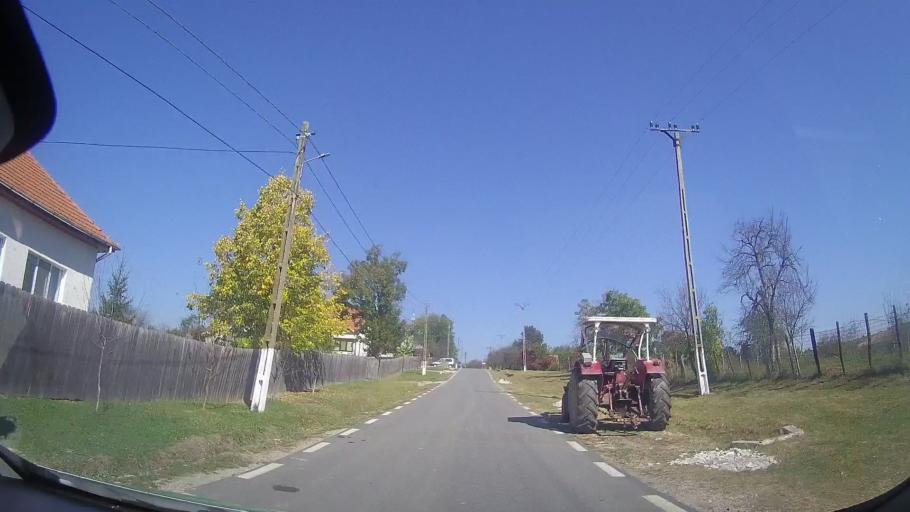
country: RO
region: Timis
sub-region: Comuna Ohaba Lunga
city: Ohaba Lunga
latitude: 45.9054
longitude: 21.9367
